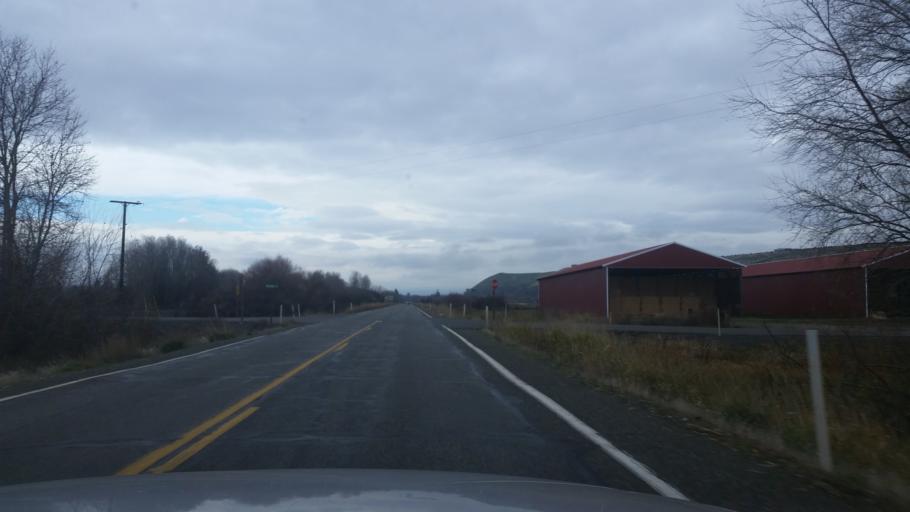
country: US
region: Washington
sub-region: Kittitas County
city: Ellensburg
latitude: 47.0427
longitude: -120.6227
